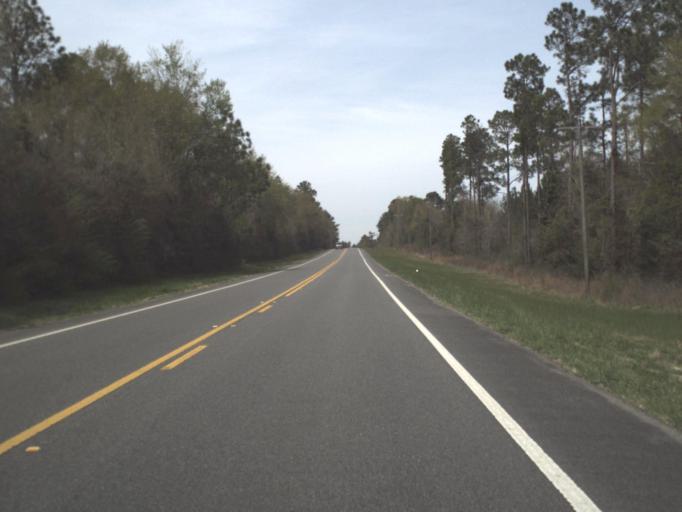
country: US
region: Alabama
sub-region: Geneva County
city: Geneva
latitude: 30.9554
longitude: -85.9881
